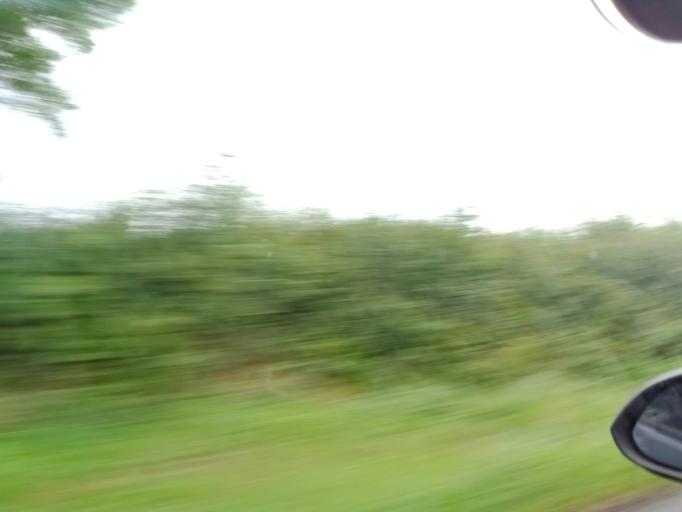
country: IE
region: Leinster
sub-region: Kilkenny
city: Castlecomer
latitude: 52.8513
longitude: -7.1754
